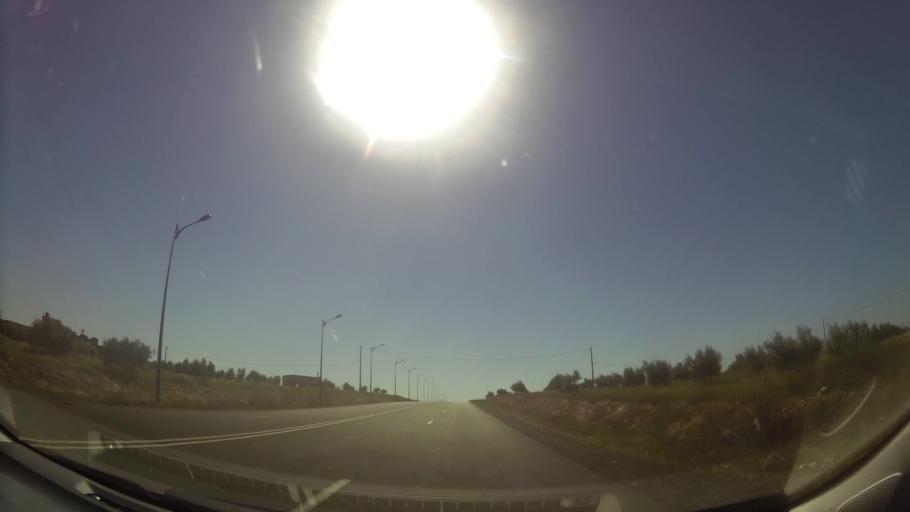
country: MA
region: Oriental
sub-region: Oujda-Angad
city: Oujda
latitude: 34.7409
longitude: -1.9024
